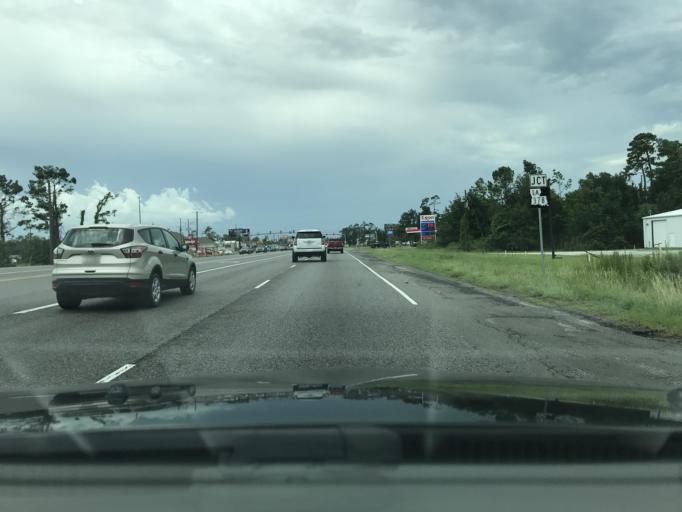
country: US
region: Louisiana
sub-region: Calcasieu Parish
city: Moss Bluff
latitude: 30.2987
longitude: -93.1952
